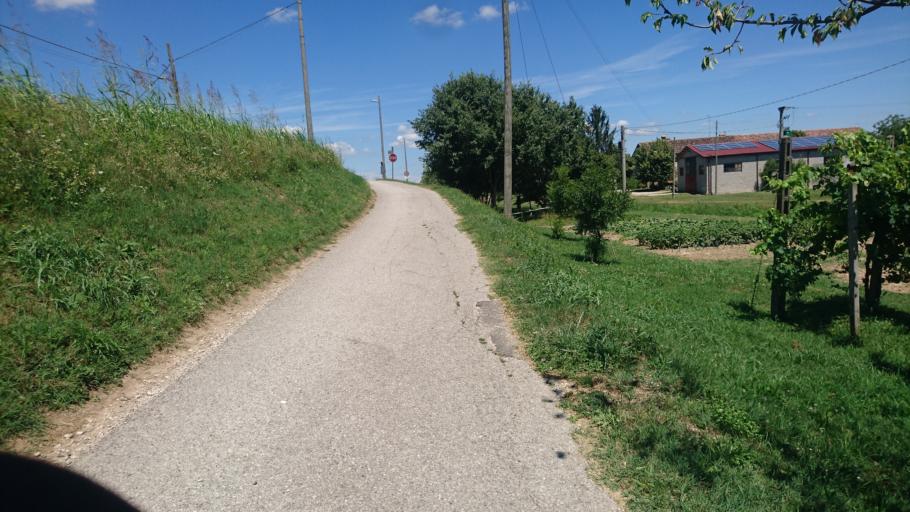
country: IT
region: Veneto
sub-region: Provincia di Padova
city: Polverara
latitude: 45.3294
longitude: 11.9454
